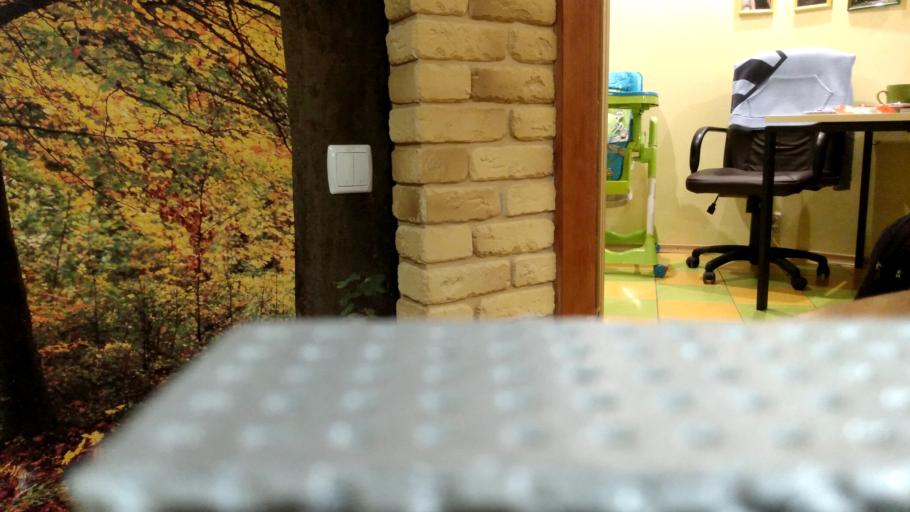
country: RU
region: Republic of Karelia
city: Pudozh
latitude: 61.8753
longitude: 37.6446
